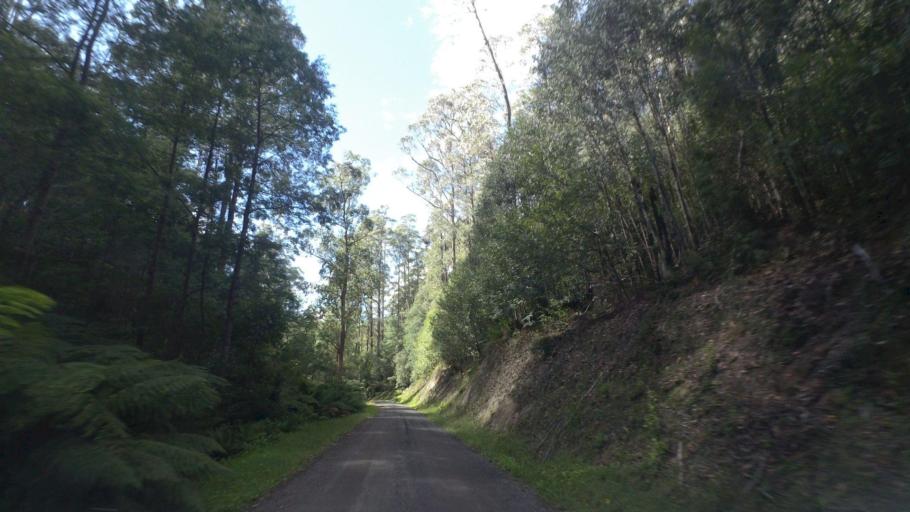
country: AU
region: Victoria
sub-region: Cardinia
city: Bunyip
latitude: -37.9582
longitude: 145.8210
